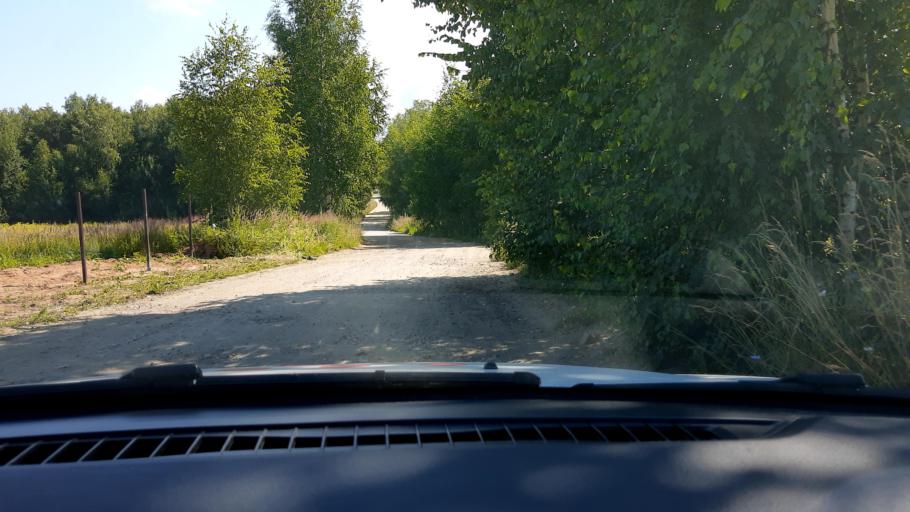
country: RU
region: Nizjnij Novgorod
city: Burevestnik
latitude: 56.0534
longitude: 43.9795
